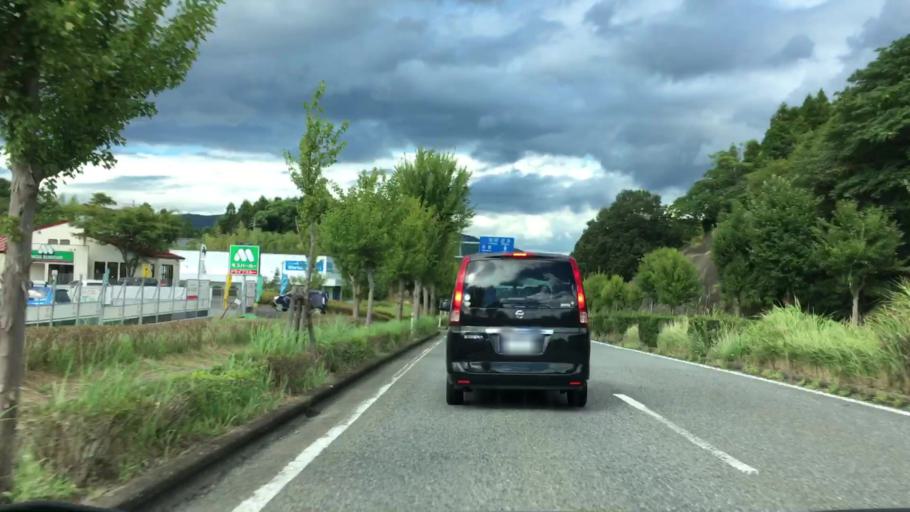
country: JP
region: Saga Prefecture
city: Imaricho-ko
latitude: 33.2670
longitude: 129.8662
